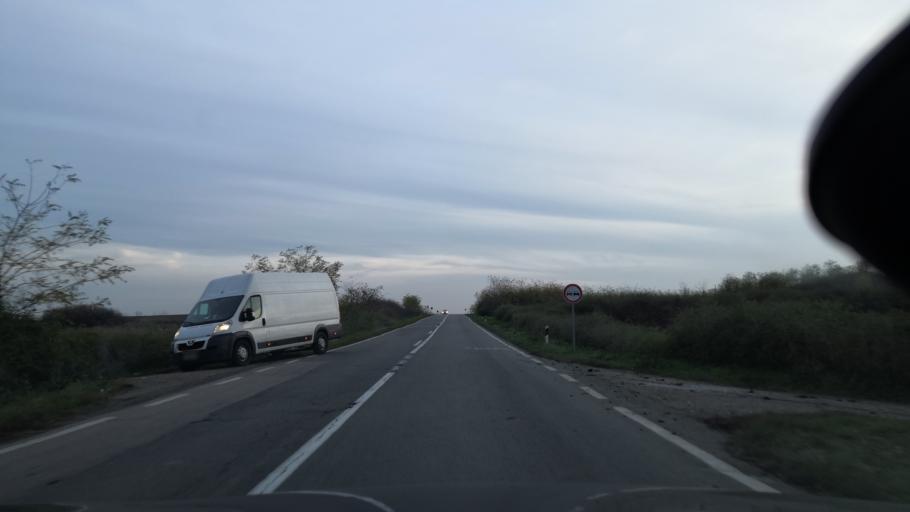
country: RS
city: Ostojicevo
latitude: 45.9049
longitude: 20.1546
